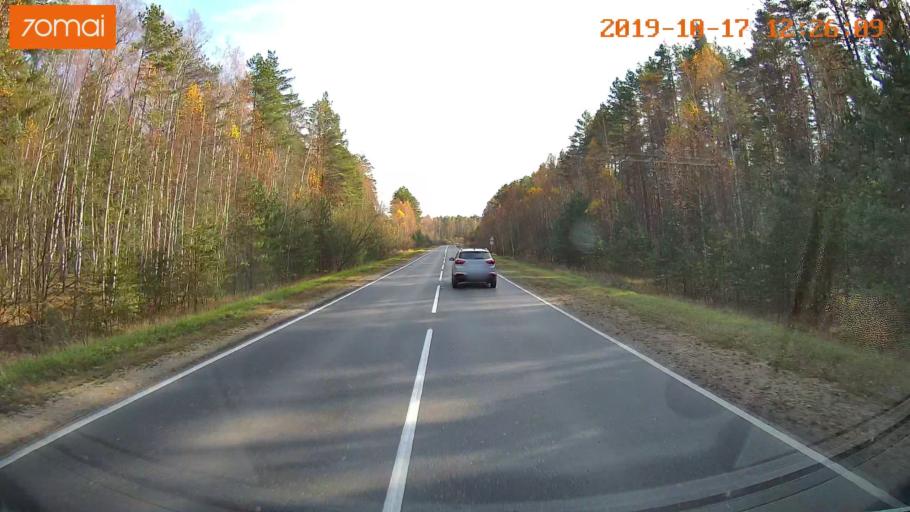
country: RU
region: Rjazan
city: Syntul
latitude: 55.0216
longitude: 41.2507
